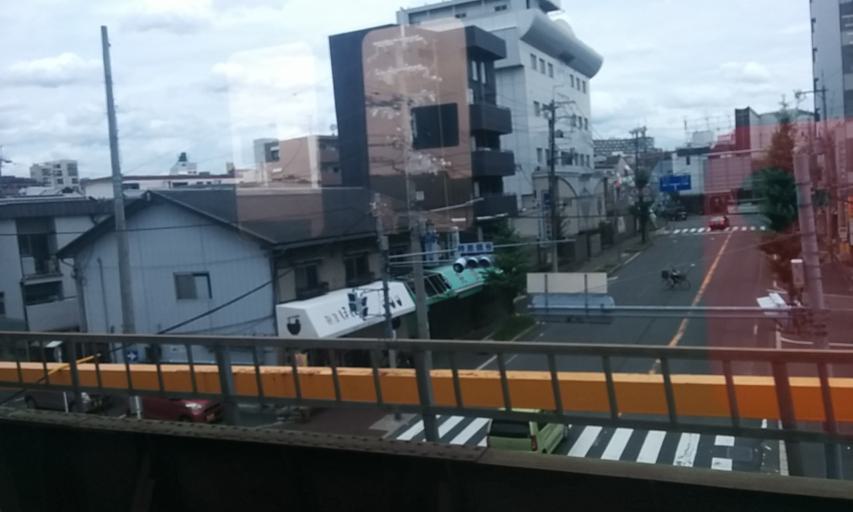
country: JP
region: Osaka
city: Mino
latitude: 34.8130
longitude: 135.4638
